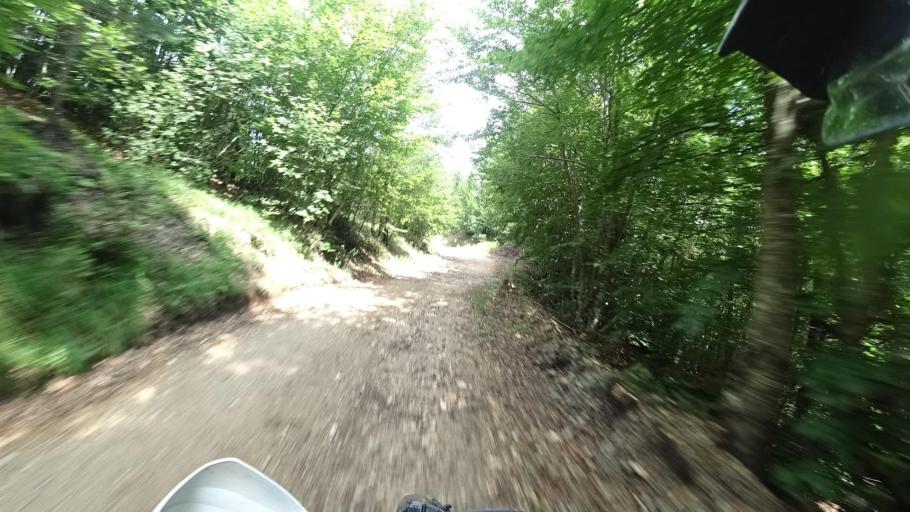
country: HR
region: Licko-Senjska
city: Otocac
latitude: 44.8792
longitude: 15.4280
